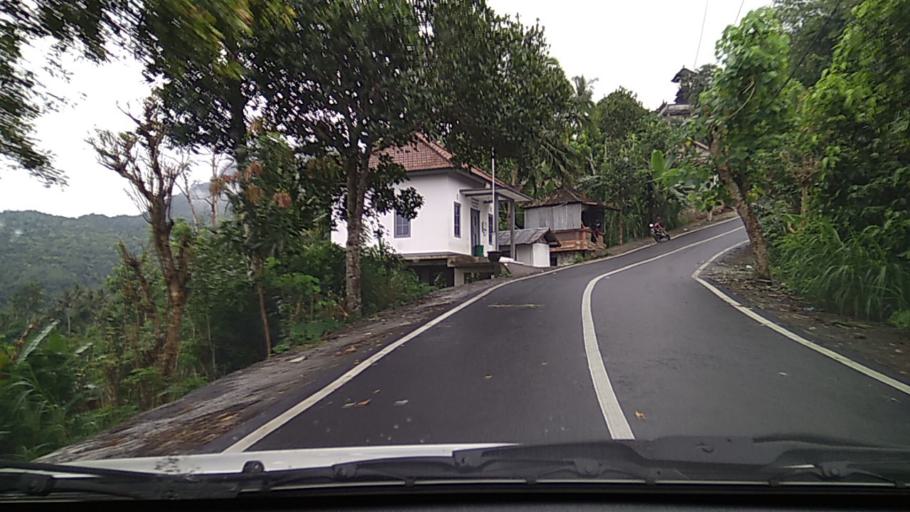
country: ID
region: Bali
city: Tistagede
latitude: -8.3904
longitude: 115.6291
